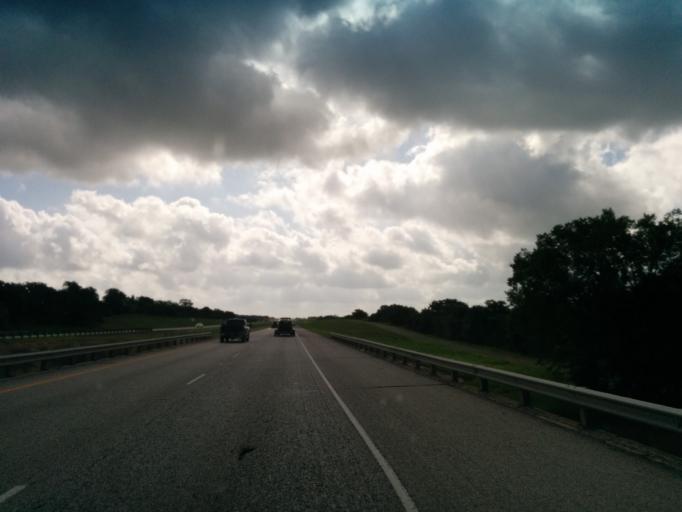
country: US
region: Texas
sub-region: Gonzales County
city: Waelder
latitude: 29.6627
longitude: -97.3799
